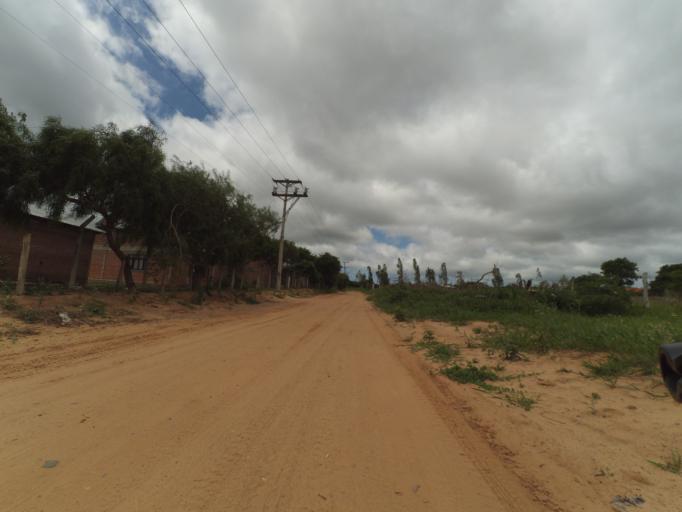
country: BO
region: Santa Cruz
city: Santa Rita
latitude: -17.9123
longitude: -63.2504
